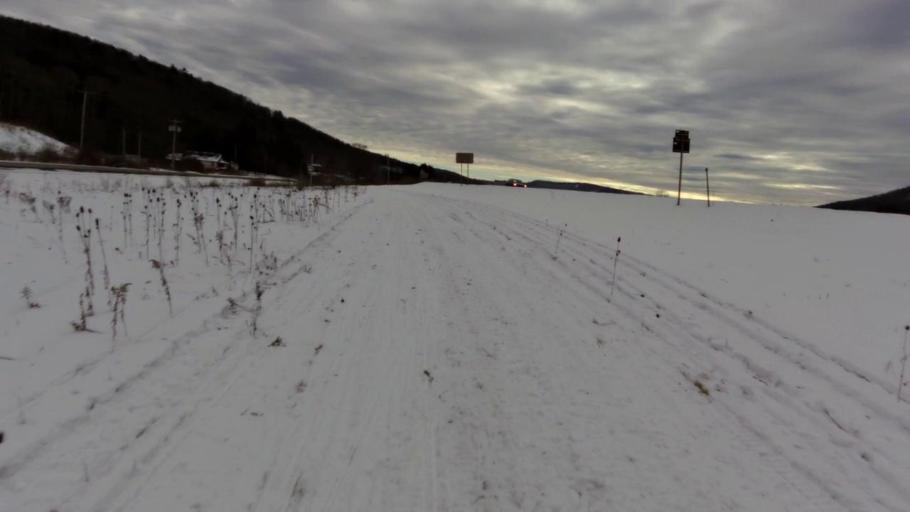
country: US
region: Pennsylvania
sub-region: McKean County
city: Foster Brook
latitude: 42.0027
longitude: -78.6192
